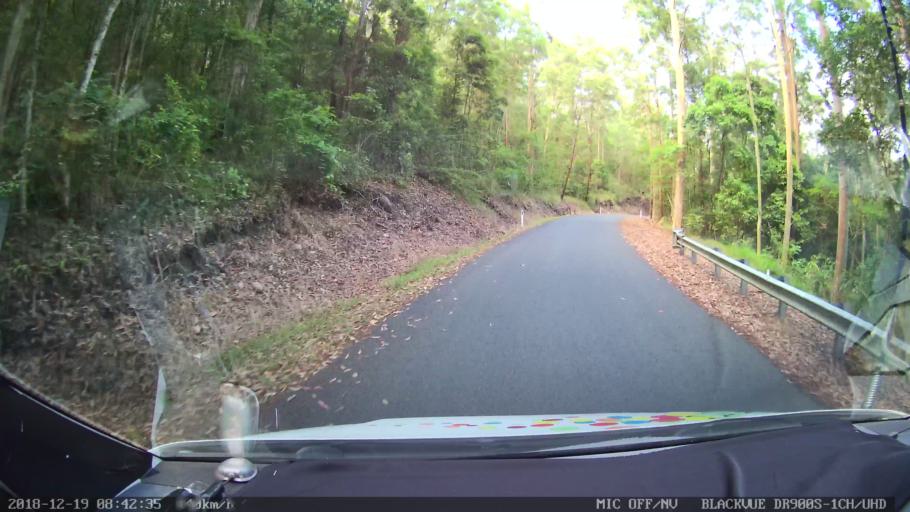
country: AU
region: New South Wales
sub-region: Kyogle
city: Kyogle
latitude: -28.3455
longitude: 152.9720
